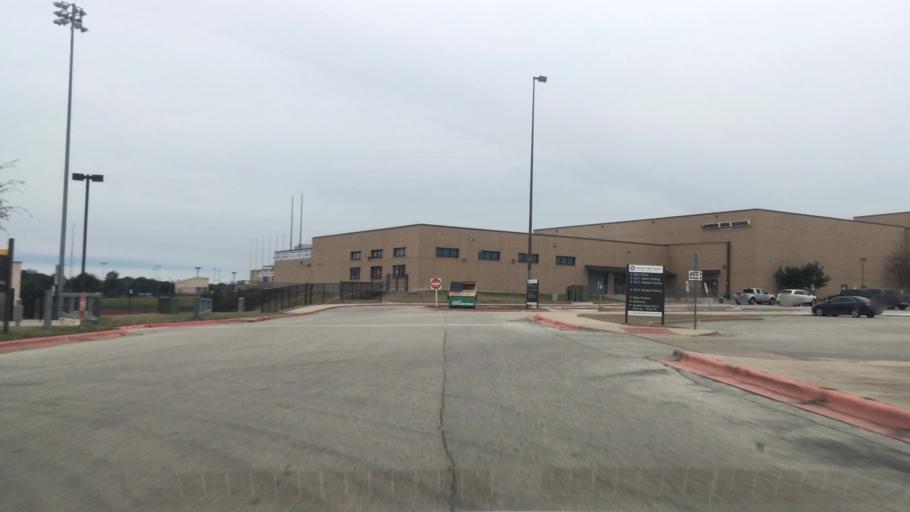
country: US
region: Texas
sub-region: Williamson County
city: Leander
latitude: 30.5379
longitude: -97.8489
